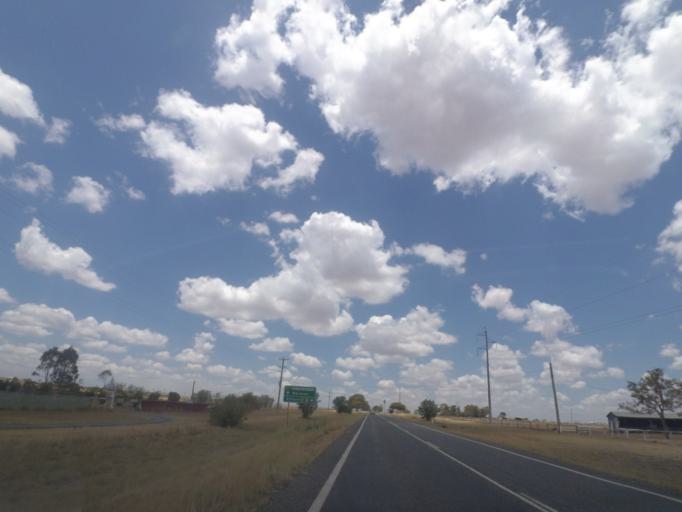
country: AU
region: Queensland
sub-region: Southern Downs
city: Warwick
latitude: -27.9295
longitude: 151.9856
